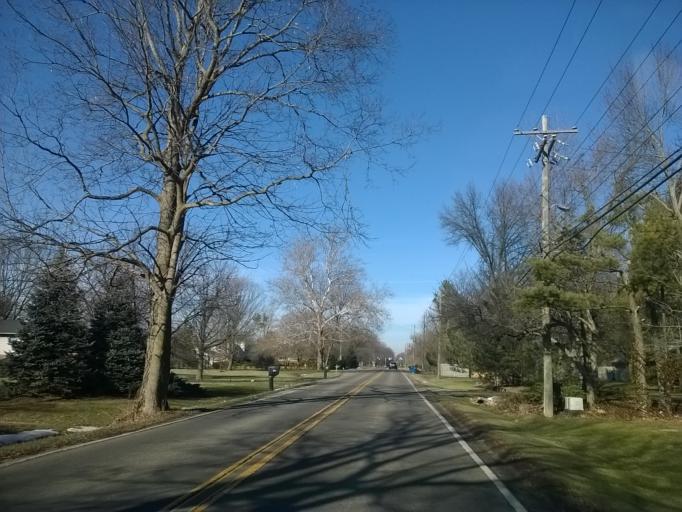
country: US
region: Indiana
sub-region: Marion County
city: Meridian Hills
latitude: 39.9088
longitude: -86.1651
